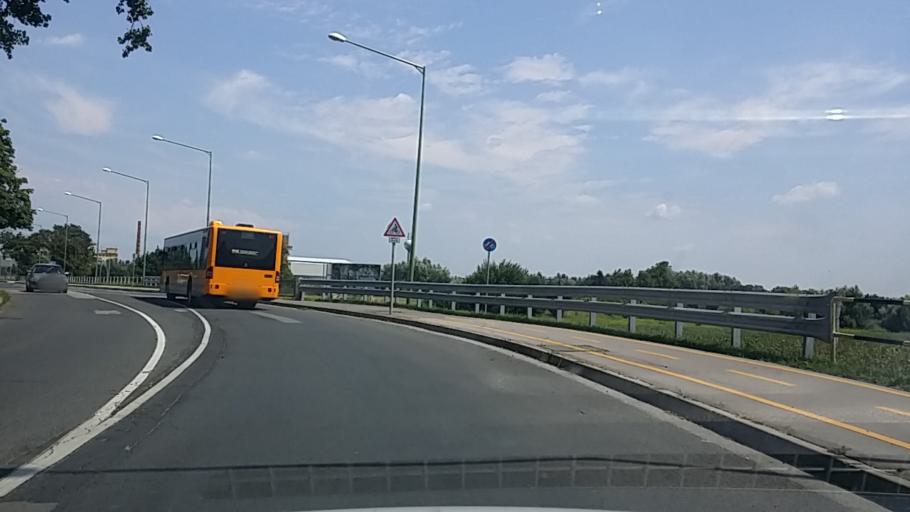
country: HU
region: Zala
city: Nagykanizsa
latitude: 46.4525
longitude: 16.9700
